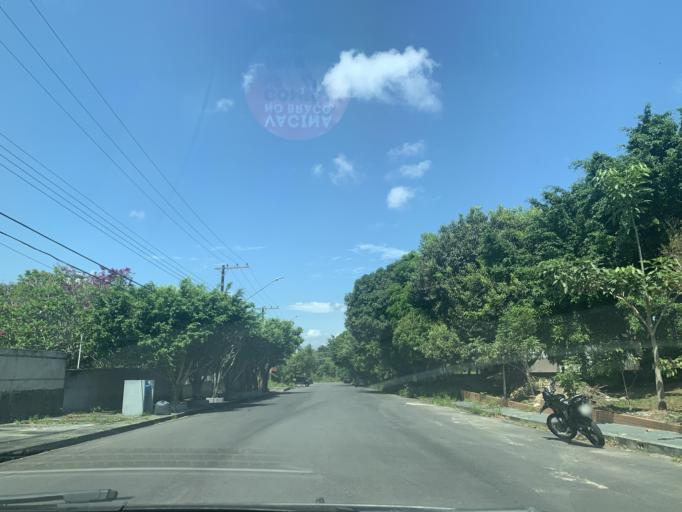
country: BR
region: Amazonas
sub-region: Manaus
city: Manaus
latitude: -3.1108
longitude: -59.9713
